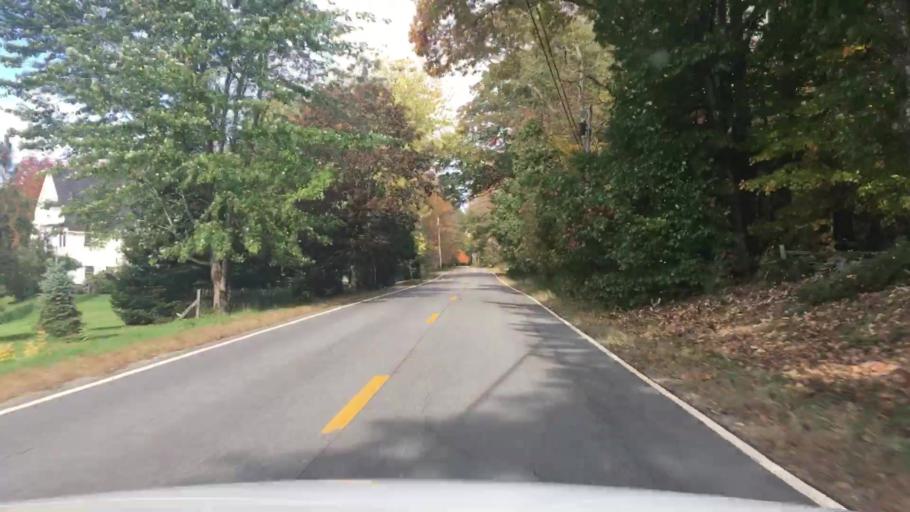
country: US
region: Maine
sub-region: Knox County
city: Hope
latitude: 44.3150
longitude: -69.1210
